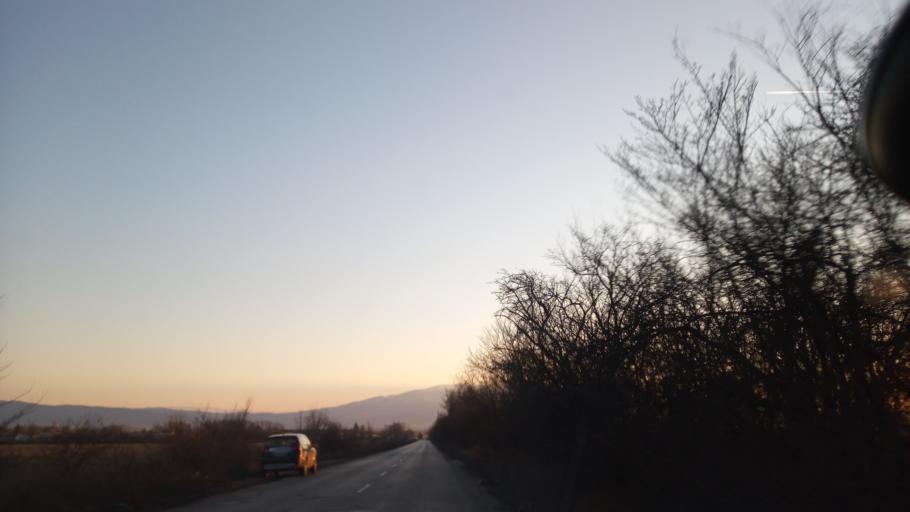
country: BG
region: Sofia-Capital
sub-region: Stolichna Obshtina
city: Bukhovo
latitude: 42.7417
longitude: 23.4728
